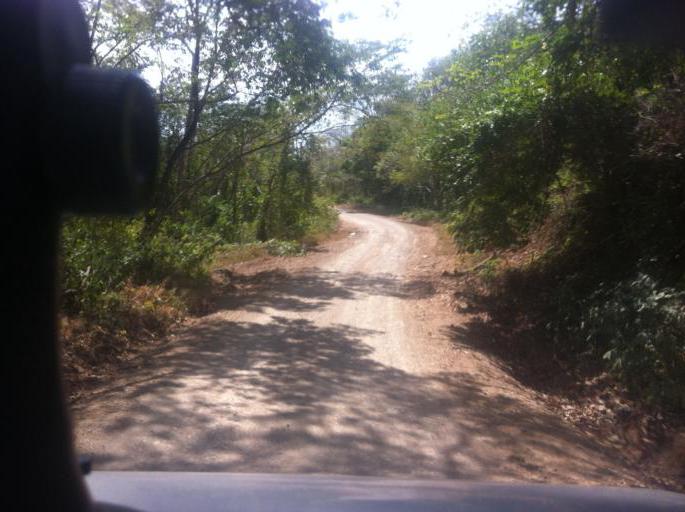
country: NI
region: Rivas
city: Belen
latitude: 11.5622
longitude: -86.0306
